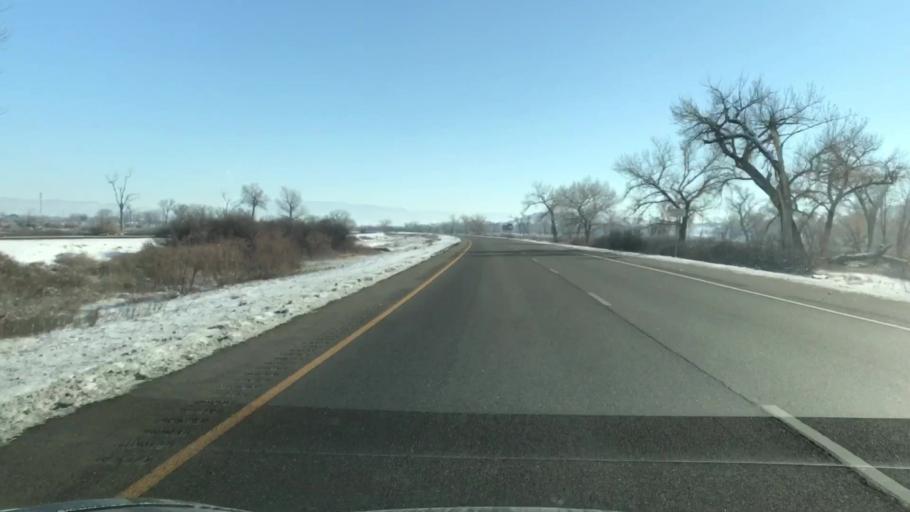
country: US
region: Colorado
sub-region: Mesa County
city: Loma
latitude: 39.1651
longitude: -108.7845
